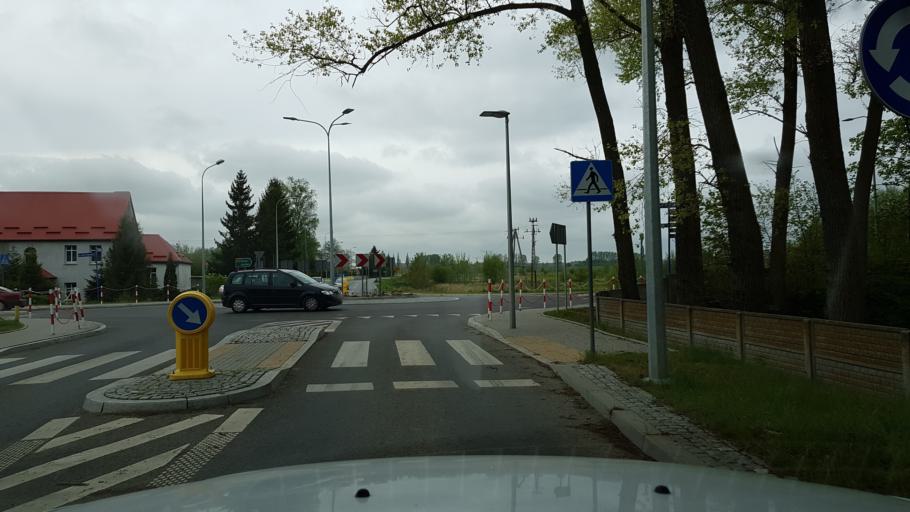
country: PL
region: West Pomeranian Voivodeship
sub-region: Powiat slawienski
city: Slawno
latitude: 54.3700
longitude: 16.6748
